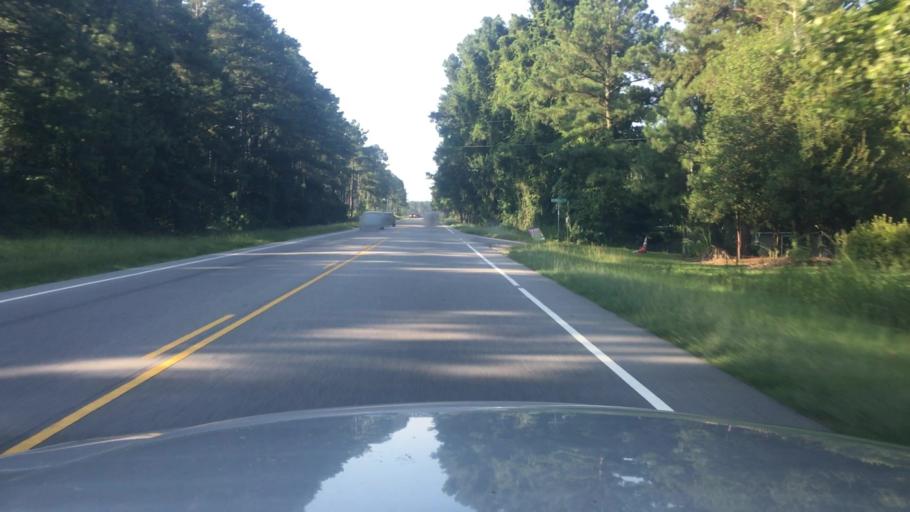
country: US
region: North Carolina
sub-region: Harnett County
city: Walkertown
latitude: 35.2004
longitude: -78.8494
